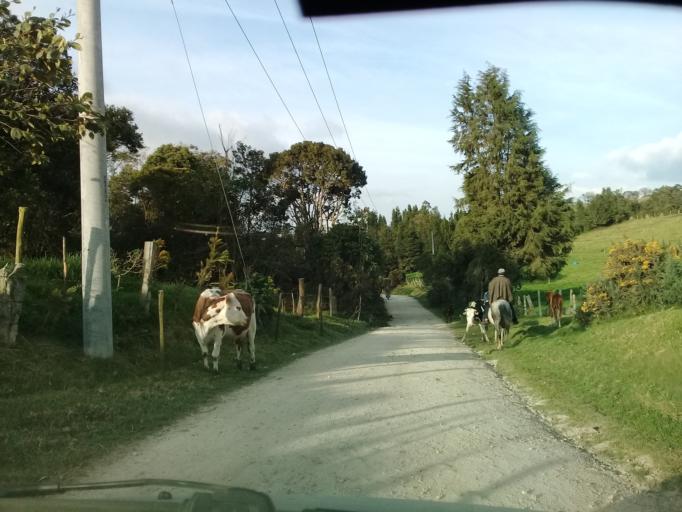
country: CO
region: Cundinamarca
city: Sibate
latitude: 4.4395
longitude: -74.2799
